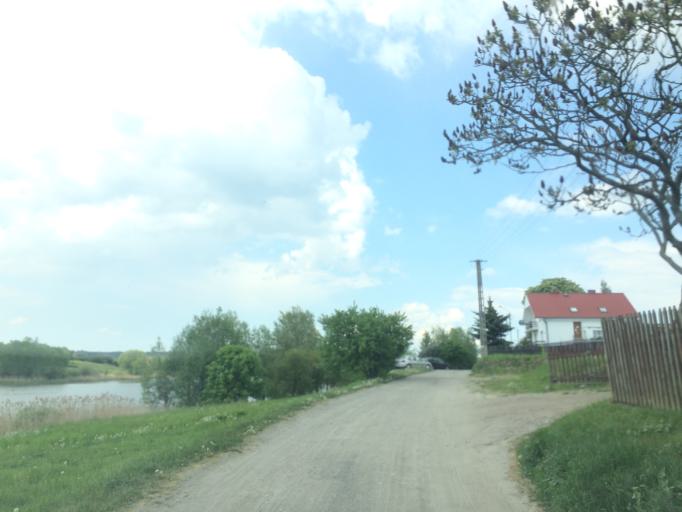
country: PL
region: Warmian-Masurian Voivodeship
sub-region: Powiat ilawski
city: Ilawa
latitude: 53.5131
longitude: 19.5683
